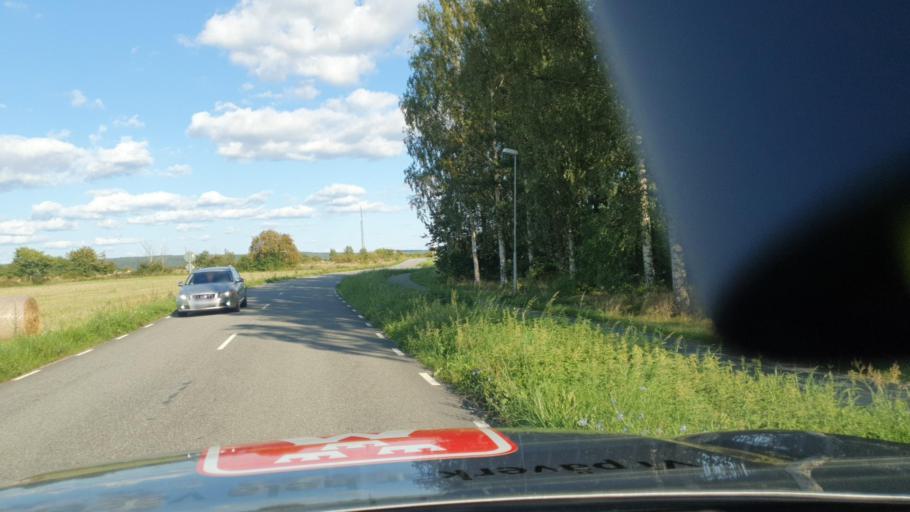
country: SE
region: Skane
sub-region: Bromolla Kommun
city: Bromoella
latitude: 56.0857
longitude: 14.4884
